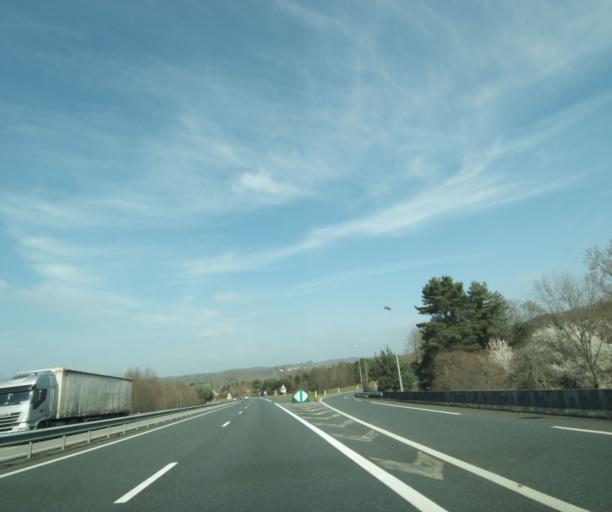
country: FR
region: Limousin
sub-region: Departement de la Haute-Vienne
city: Bessines-sur-Gartempe
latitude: 46.1088
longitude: 1.3741
